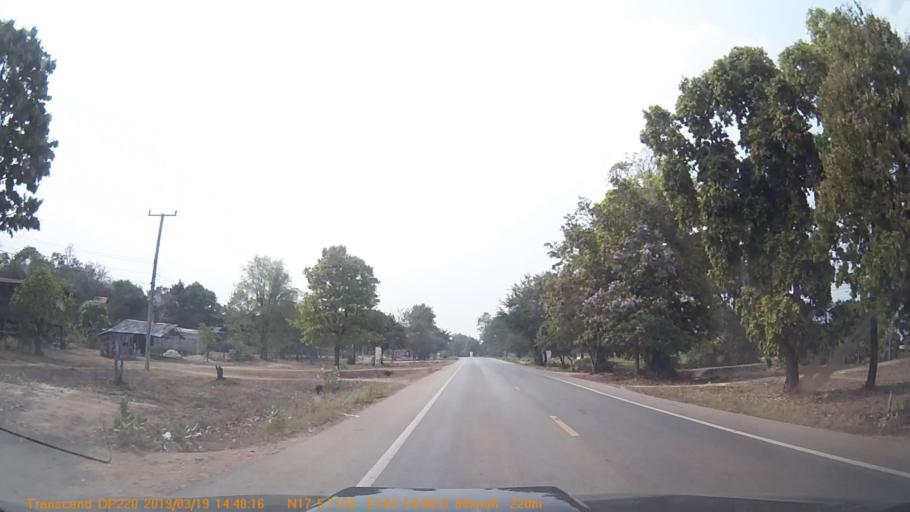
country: TH
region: Sakon Nakhon
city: Kut Bak
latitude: 17.0954
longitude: 103.9161
